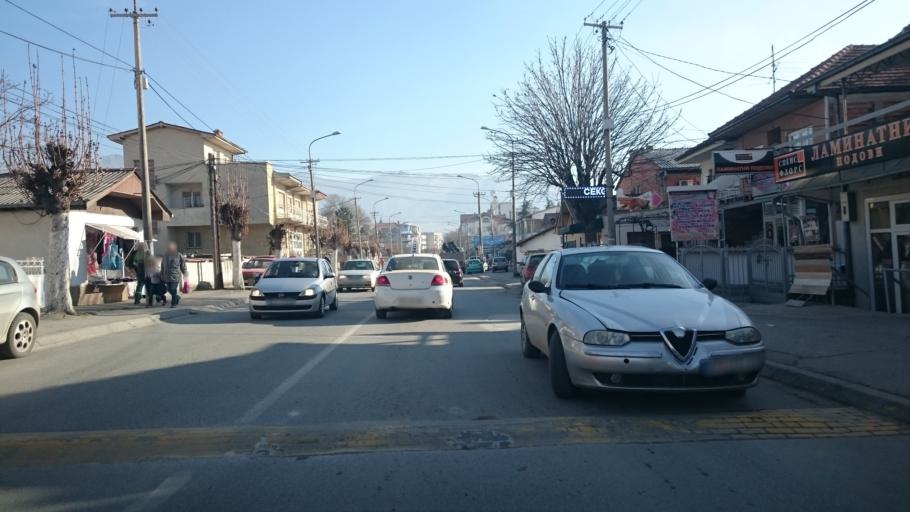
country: MK
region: Prilep
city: Prilep
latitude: 41.3497
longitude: 21.5497
